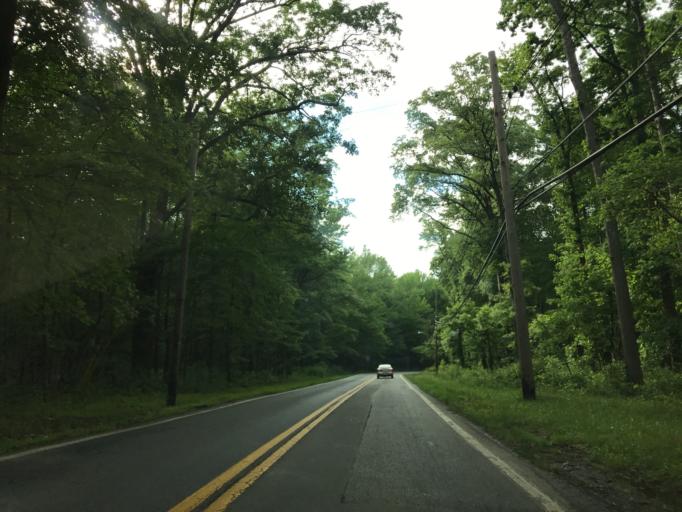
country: US
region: Maryland
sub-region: Baltimore County
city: Edgemere
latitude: 39.2775
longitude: -76.4218
